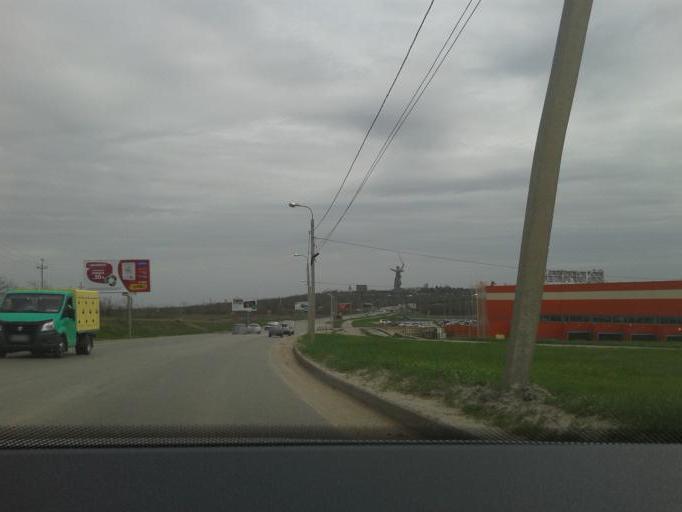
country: RU
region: Volgograd
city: Volgograd
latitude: 48.7462
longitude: 44.5173
